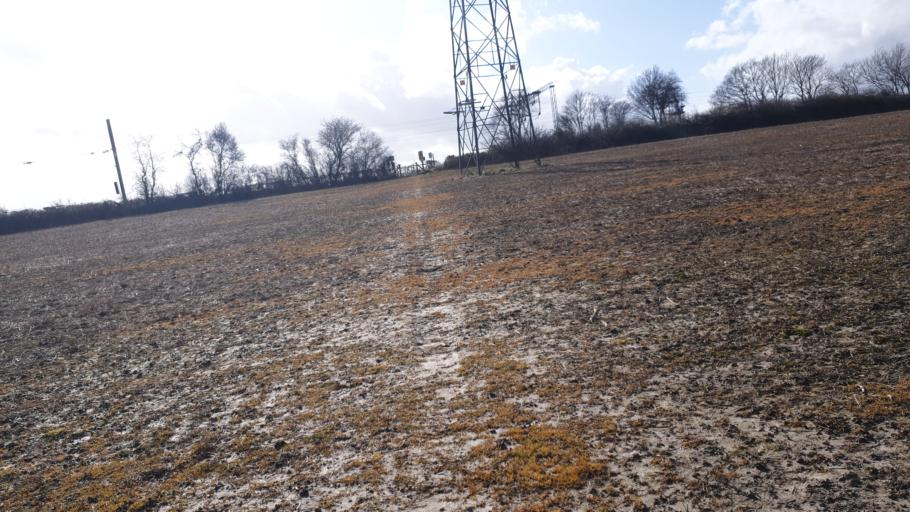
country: GB
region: England
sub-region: Essex
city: Little Clacton
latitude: 51.8508
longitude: 1.1534
